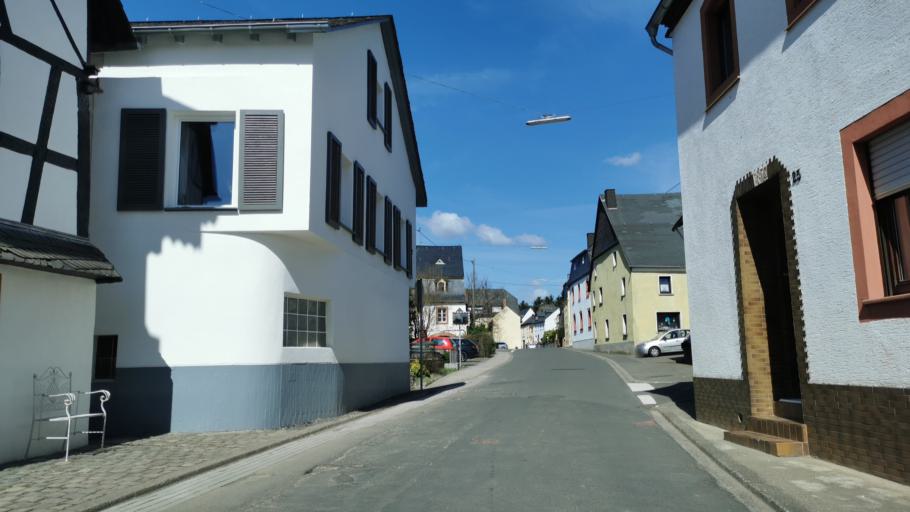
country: DE
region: Rheinland-Pfalz
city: Maring-Noviand
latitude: 49.9253
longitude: 7.0025
